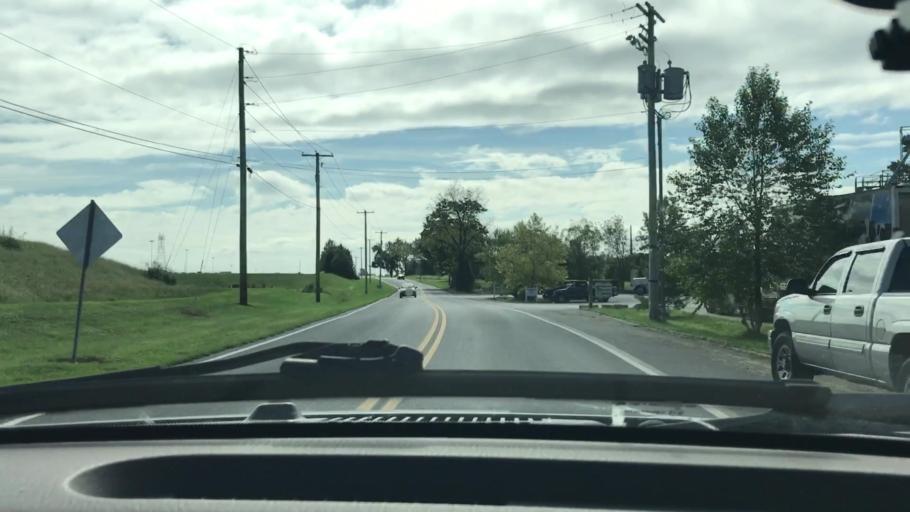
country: US
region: Pennsylvania
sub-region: Lancaster County
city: Manheim
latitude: 40.1416
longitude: -76.4080
